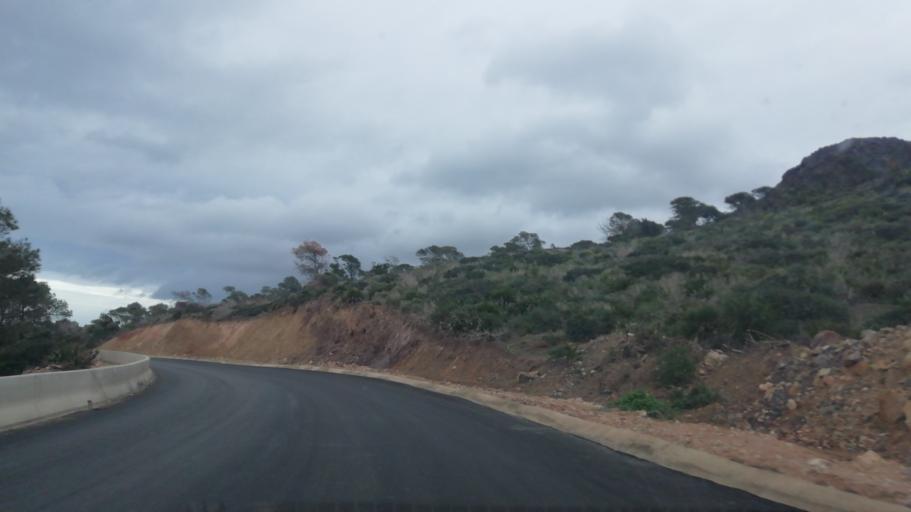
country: DZ
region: Oran
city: Bir el Djir
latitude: 35.7753
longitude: -0.5134
